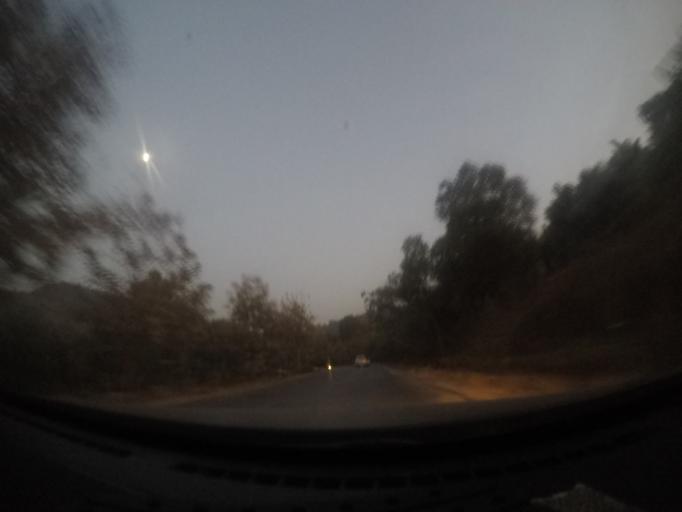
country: MM
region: Mandalay
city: Yamethin
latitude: 20.7055
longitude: 96.5089
